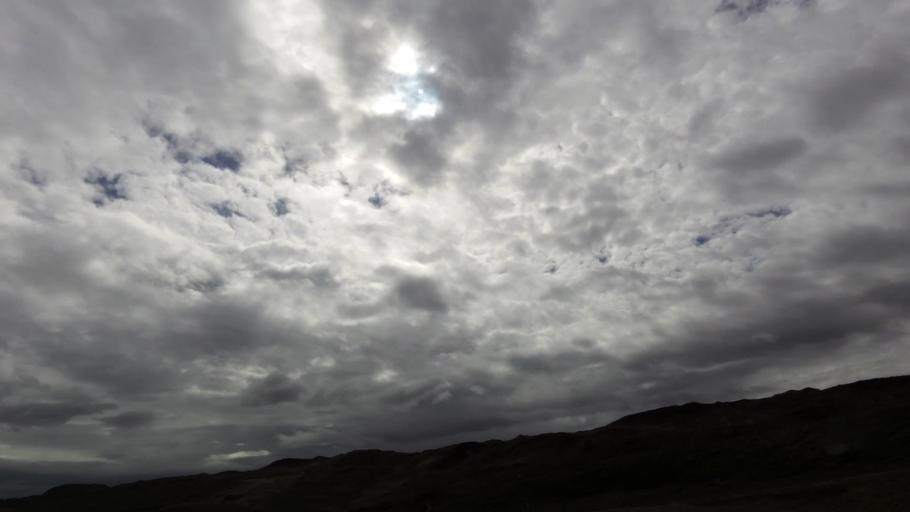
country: IS
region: West
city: Stykkisholmur
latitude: 65.5384
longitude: -22.1170
